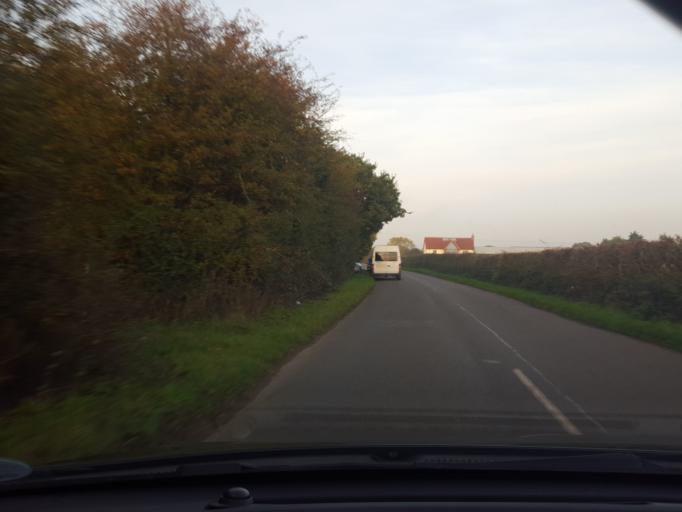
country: GB
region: England
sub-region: Essex
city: Little Clacton
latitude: 51.8299
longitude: 1.1142
